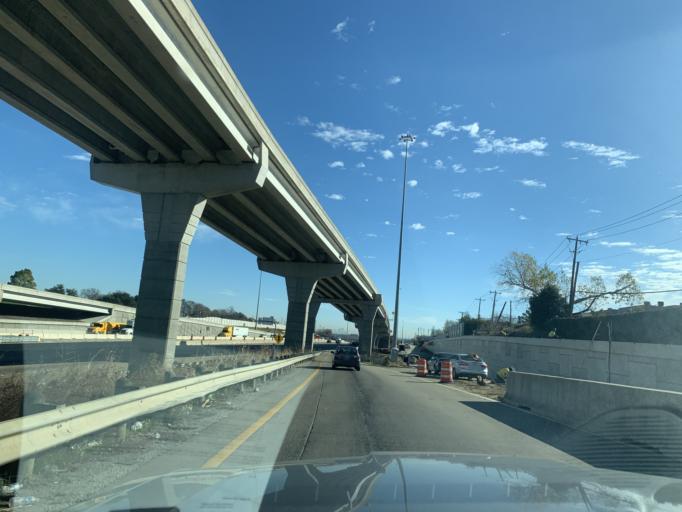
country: US
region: Texas
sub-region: Dallas County
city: Grand Prairie
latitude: 32.7590
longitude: -97.0270
